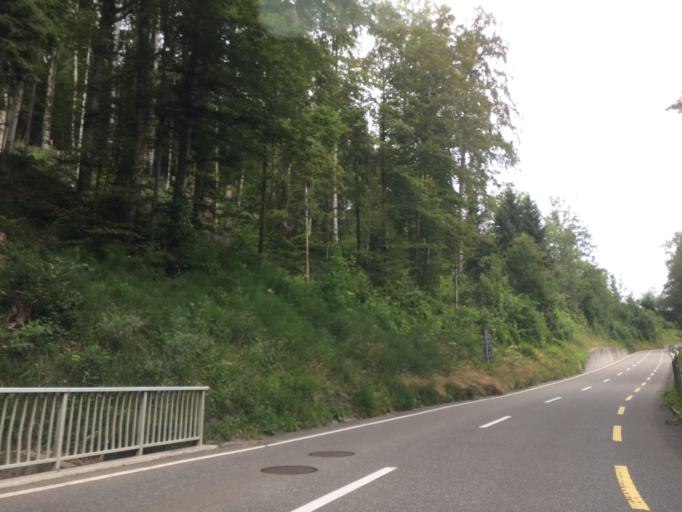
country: CH
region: Appenzell Ausserrhoden
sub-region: Bezirk Mittelland
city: Trogen
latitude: 47.4055
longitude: 9.4665
